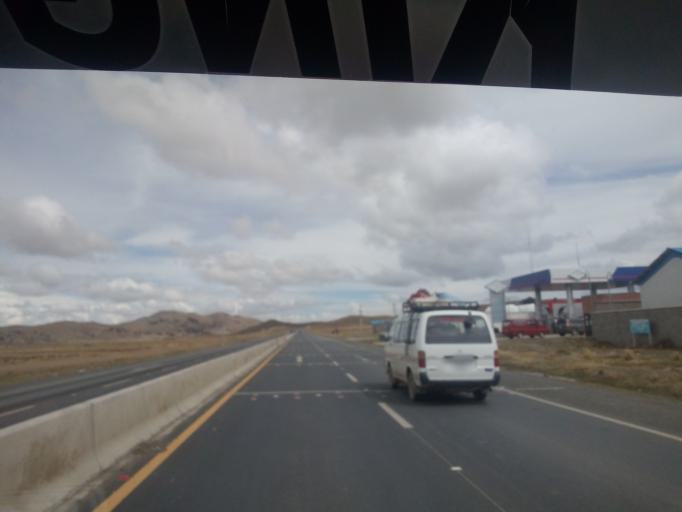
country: BO
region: La Paz
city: Achacachi
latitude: -16.0785
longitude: -68.6725
